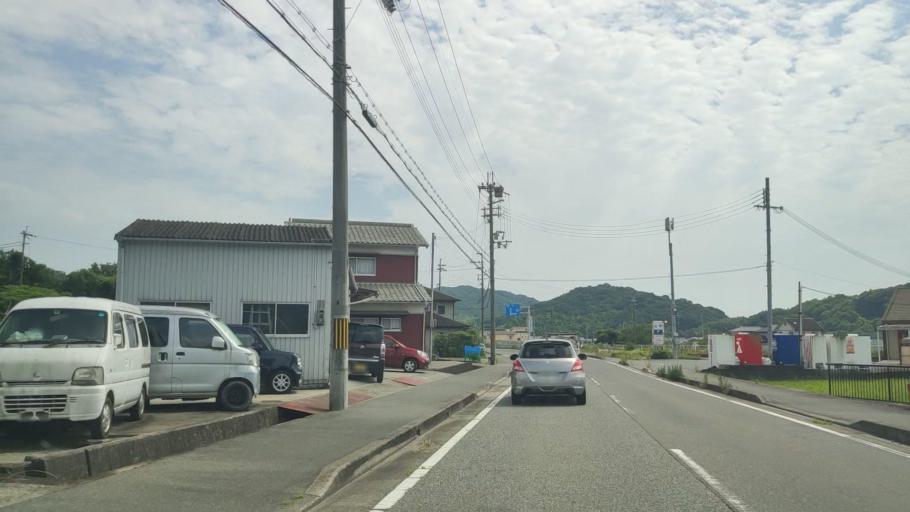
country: JP
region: Hyogo
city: Tatsunocho-tominaga
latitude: 34.8435
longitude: 134.5995
